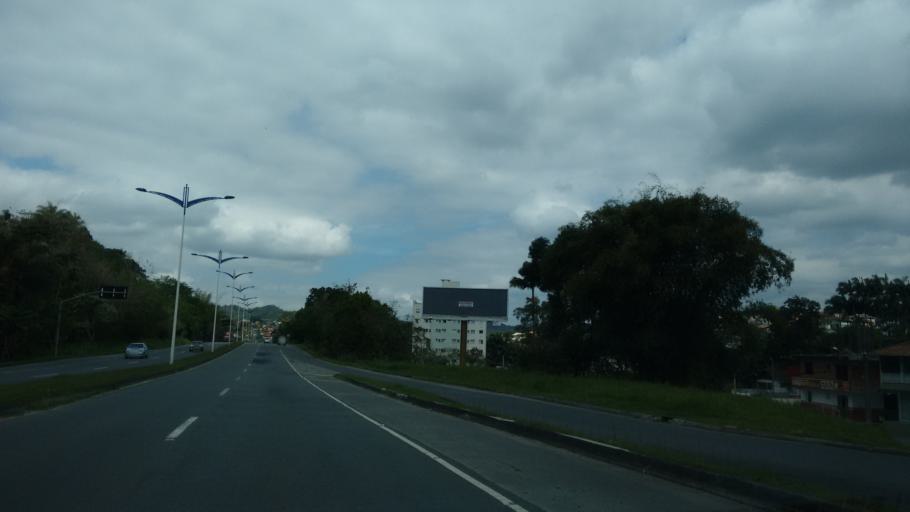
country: BR
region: Santa Catarina
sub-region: Blumenau
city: Blumenau
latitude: -26.8709
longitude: -49.0717
